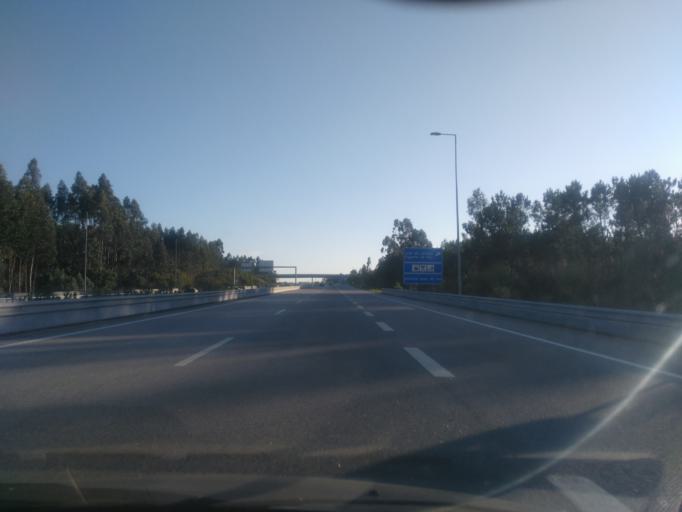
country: PT
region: Coimbra
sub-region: Figueira da Foz
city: Alhadas
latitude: 40.2193
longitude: -8.8029
